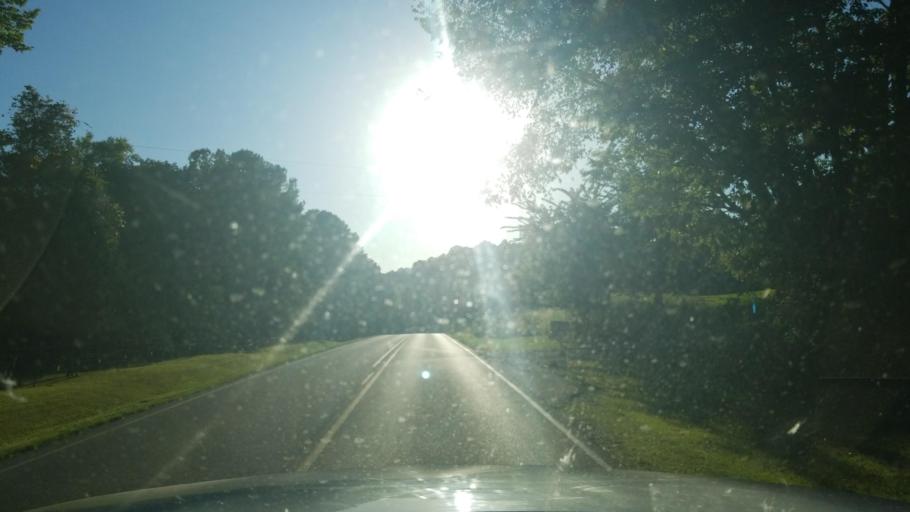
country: US
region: Illinois
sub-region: Hardin County
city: Elizabethtown
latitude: 37.5772
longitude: -88.3833
